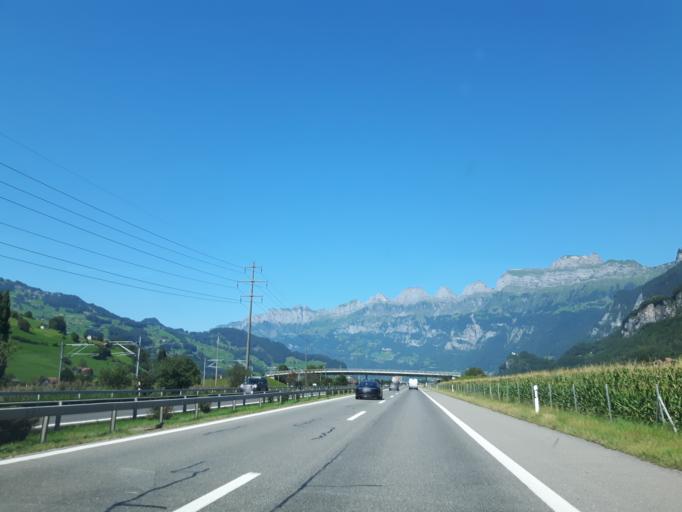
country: CH
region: Saint Gallen
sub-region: Wahlkreis Sarganserland
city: Flums
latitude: 47.0782
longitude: 9.3727
